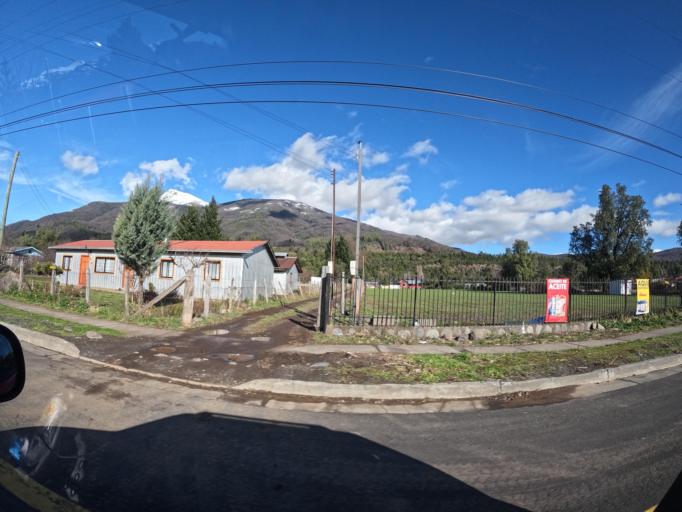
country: CL
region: Biobio
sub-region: Provincia de Biobio
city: Mulchen
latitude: -37.3295
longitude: -71.6562
